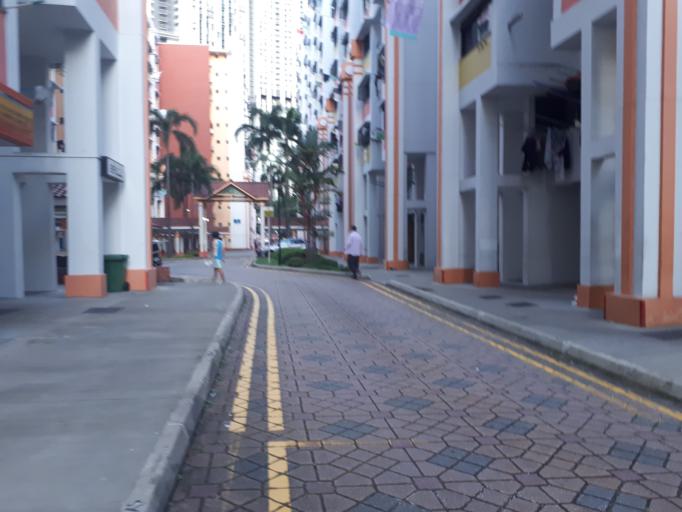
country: SG
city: Singapore
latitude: 1.2770
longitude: 103.8389
